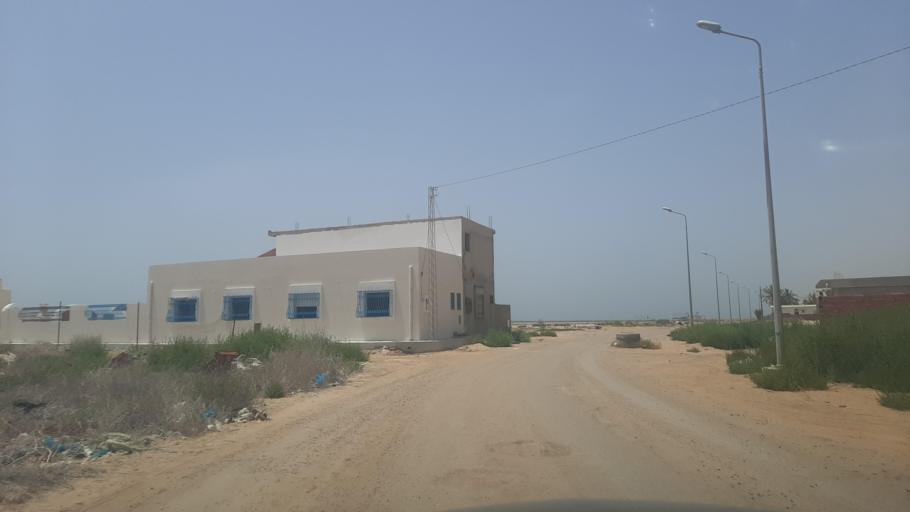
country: TN
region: Safaqis
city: Al Qarmadah
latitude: 34.7007
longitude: 11.1985
